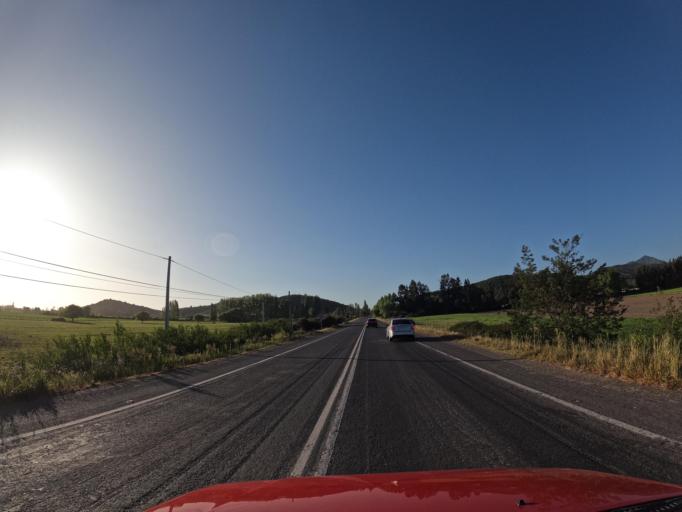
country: CL
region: O'Higgins
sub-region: Provincia de Colchagua
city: Santa Cruz
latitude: -34.4306
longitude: -71.3709
